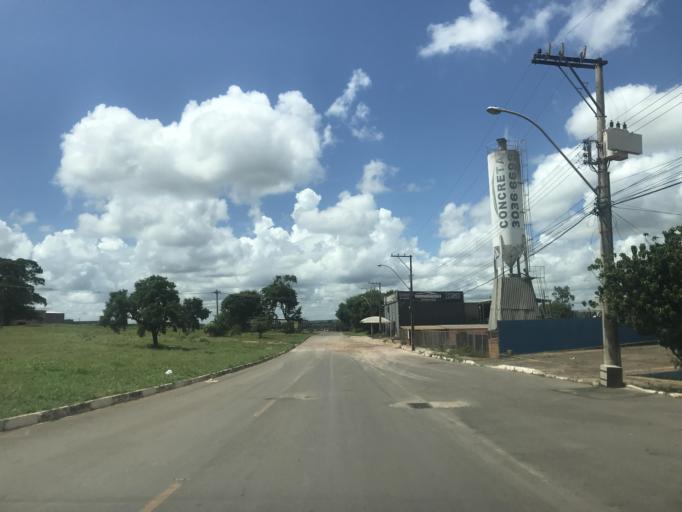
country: BR
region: Federal District
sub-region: Brasilia
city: Brasilia
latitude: -15.6578
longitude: -47.7868
